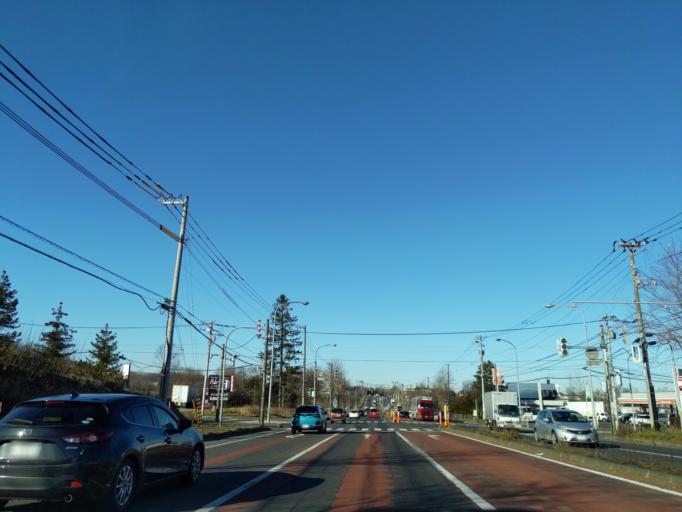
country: JP
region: Hokkaido
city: Kitahiroshima
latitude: 42.9473
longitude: 141.4999
